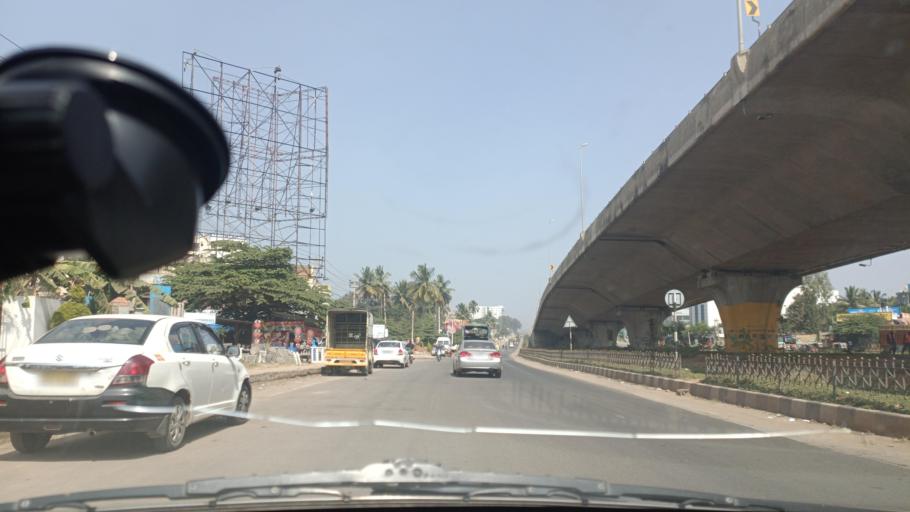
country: IN
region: Karnataka
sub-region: Bangalore Urban
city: Yelahanka
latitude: 13.1048
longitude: 77.6006
